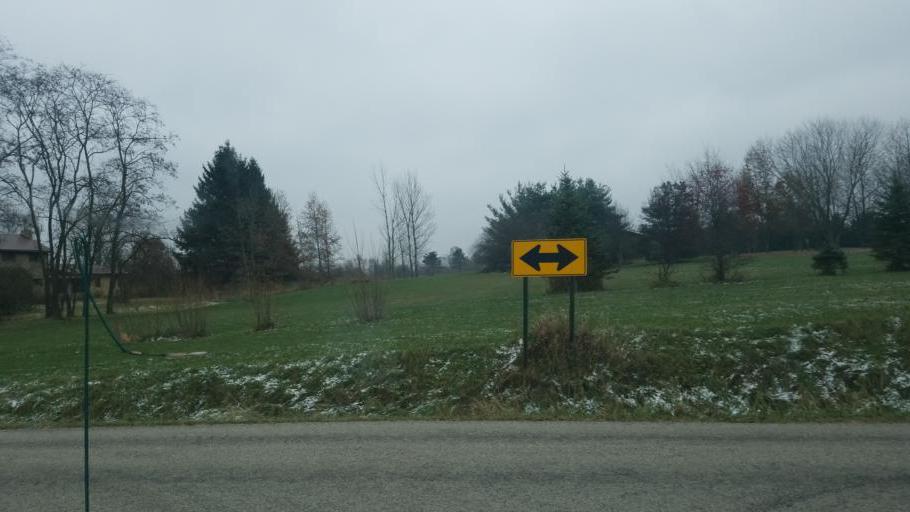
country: US
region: Ohio
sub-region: Huron County
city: New London
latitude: 41.0157
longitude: -82.3257
